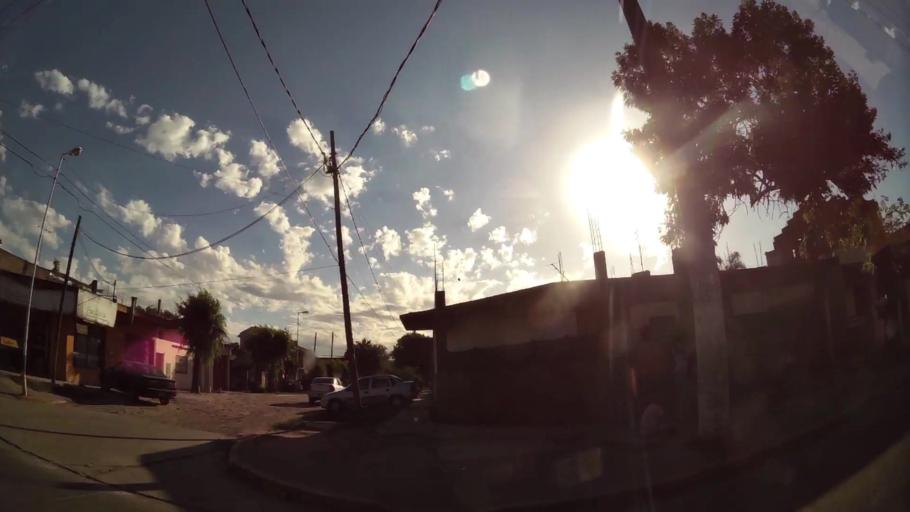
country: AR
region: Buenos Aires
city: Santa Catalina - Dique Lujan
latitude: -34.4976
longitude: -58.7178
